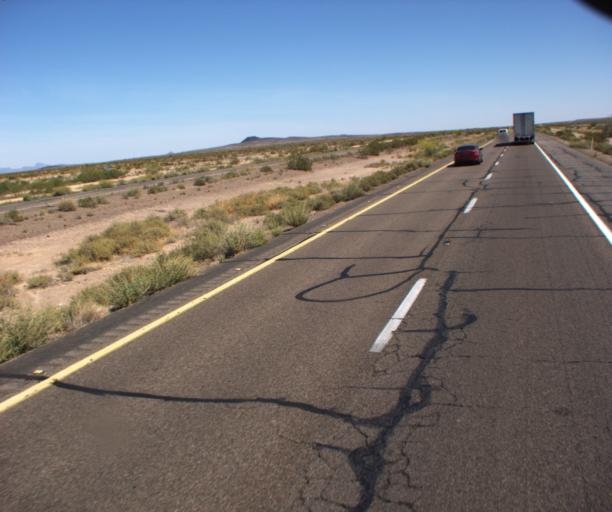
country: US
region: Arizona
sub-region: Maricopa County
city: Gila Bend
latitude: 32.8606
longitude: -113.1887
